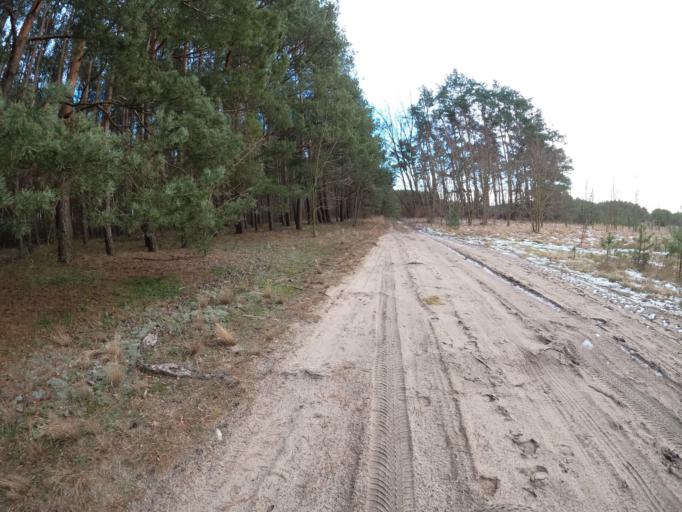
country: PL
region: Lubusz
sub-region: Powiat slubicki
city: Cybinka
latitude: 52.2139
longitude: 14.8433
